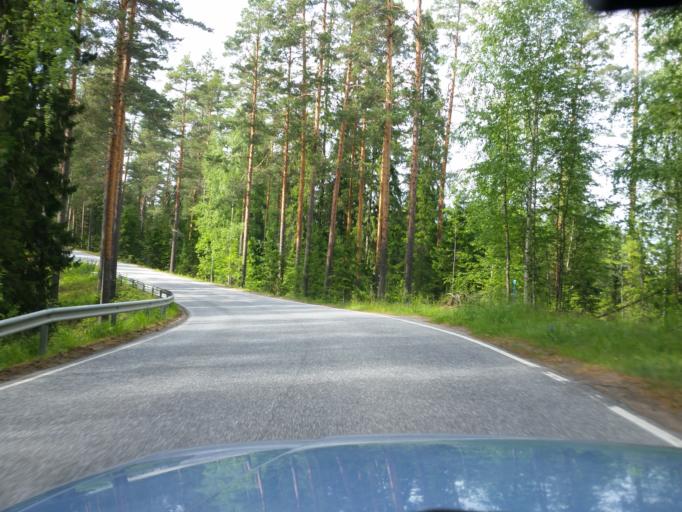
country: FI
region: Southern Savonia
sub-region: Savonlinna
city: Sulkava
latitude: 61.7922
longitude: 28.4231
